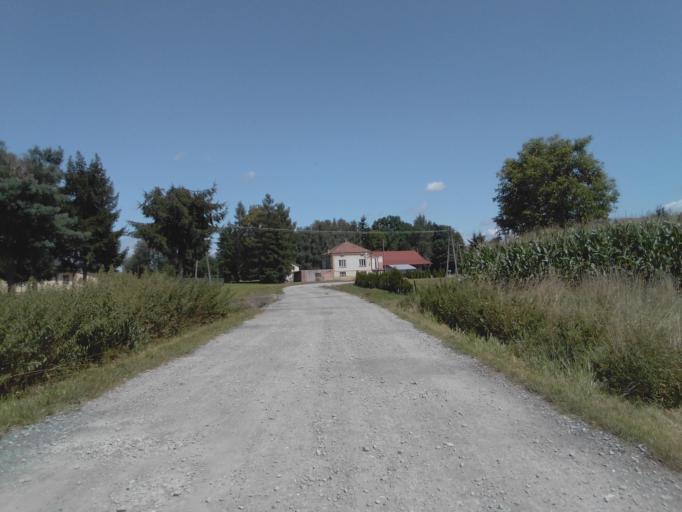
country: PL
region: Subcarpathian Voivodeship
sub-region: Powiat krosnienski
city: Wojaszowka
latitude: 49.7660
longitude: 21.6440
